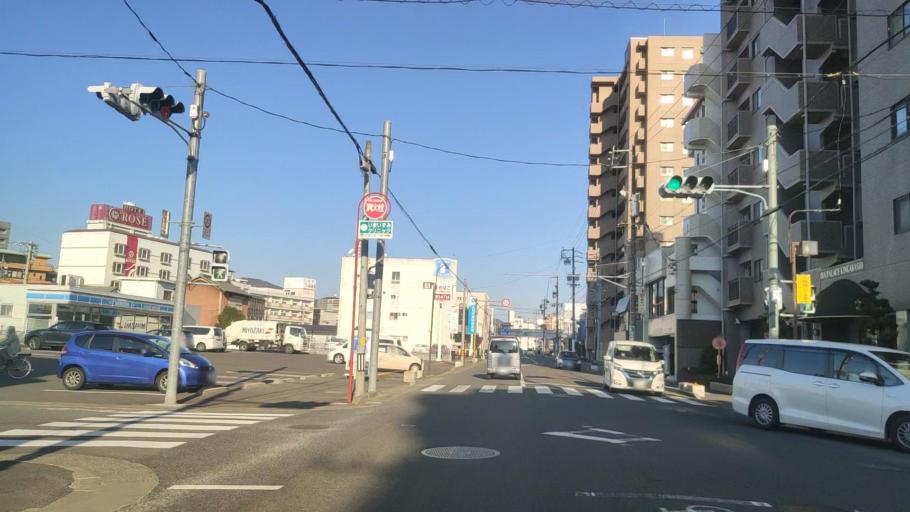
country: JP
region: Gifu
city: Gifu-shi
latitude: 35.4365
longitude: 136.7584
